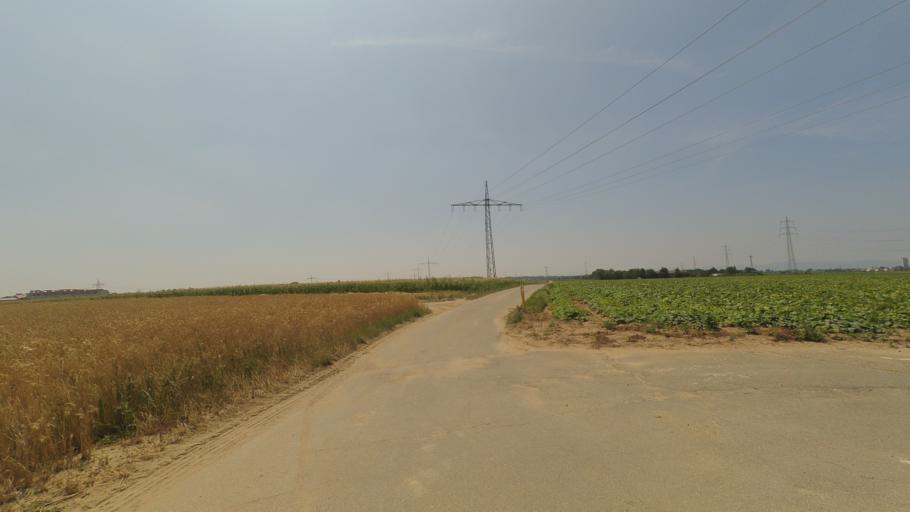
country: DE
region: Rheinland-Pfalz
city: Limburgerhof
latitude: 49.4346
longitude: 8.3892
